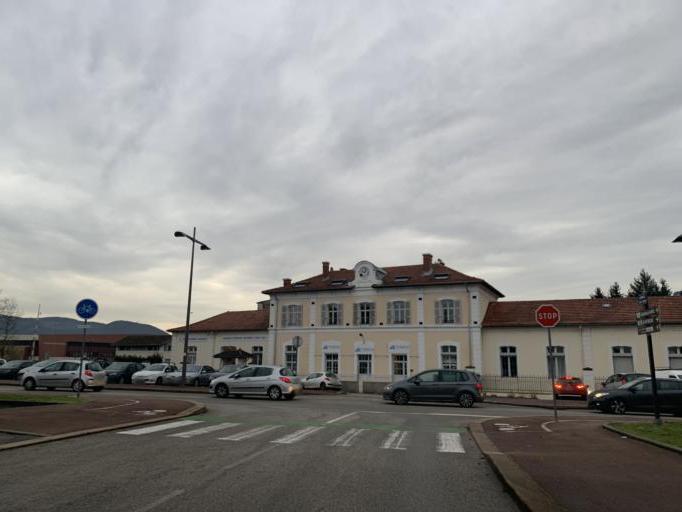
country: FR
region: Rhone-Alpes
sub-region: Departement de l'Ain
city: Belley
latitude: 45.7580
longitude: 5.6965
